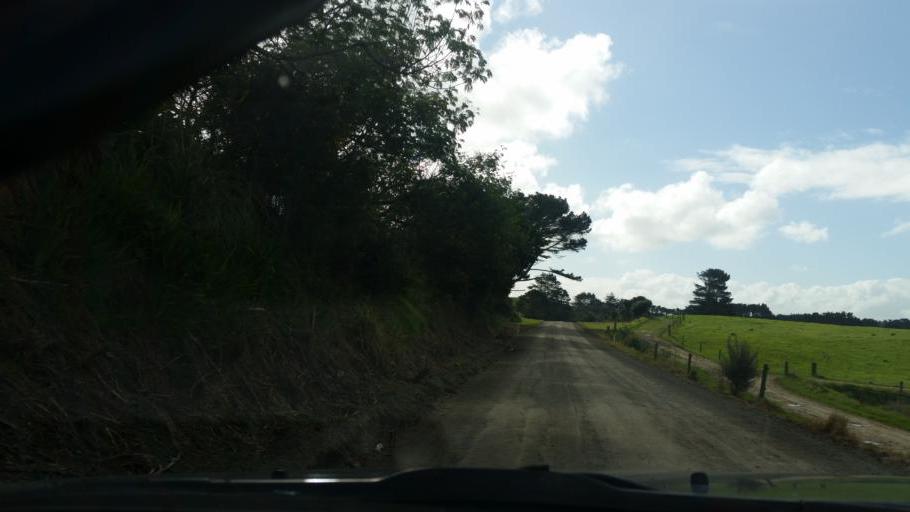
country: NZ
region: Northland
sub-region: Kaipara District
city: Dargaville
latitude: -36.0669
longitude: 173.8785
